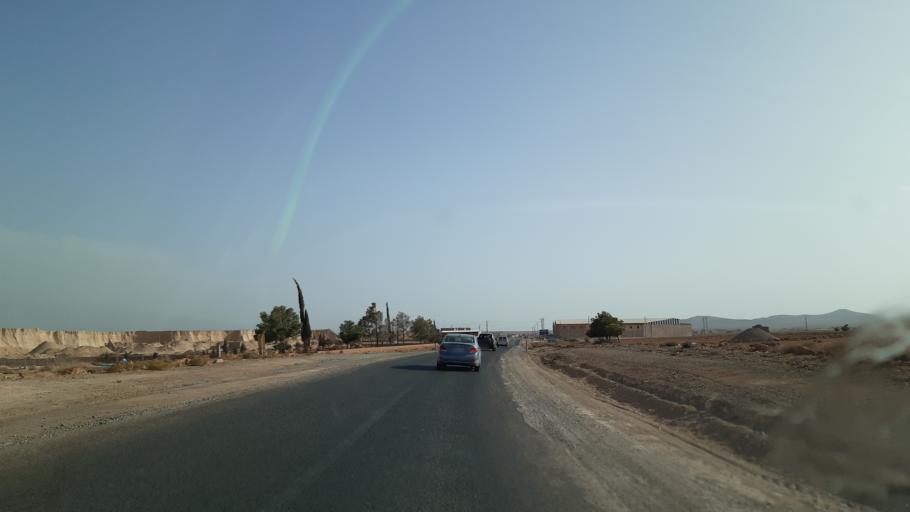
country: MA
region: Meknes-Tafilalet
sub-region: Khenifra
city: Itzer
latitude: 32.8437
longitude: -4.9524
